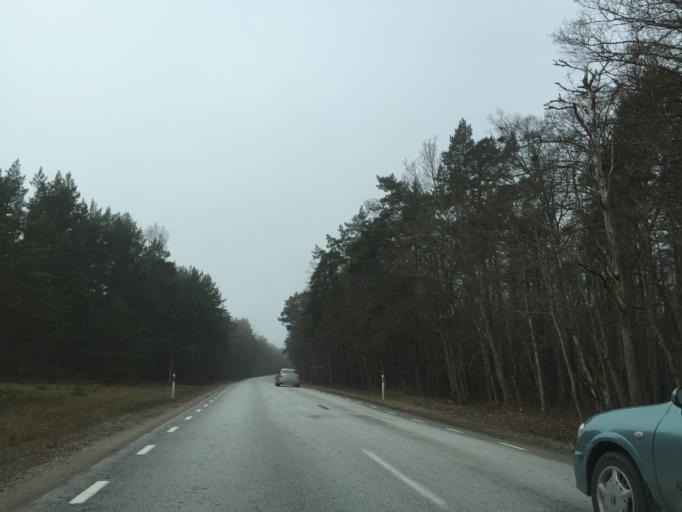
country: EE
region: Saare
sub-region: Kuressaare linn
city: Kuressaare
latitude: 58.2074
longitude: 22.3026
